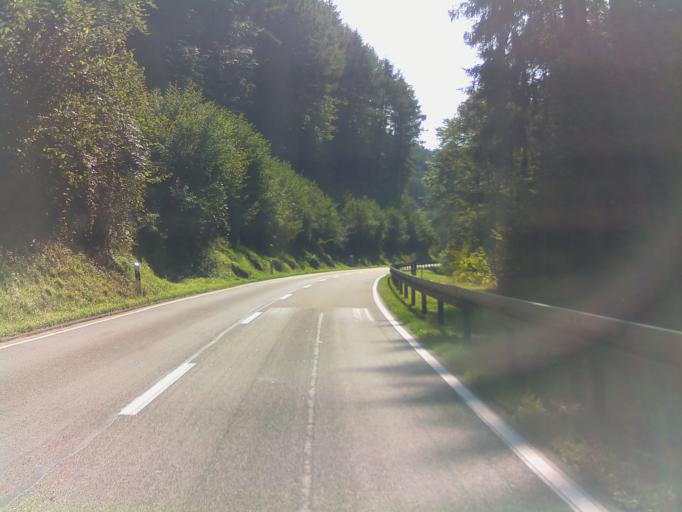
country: DE
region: Hesse
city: Hirschhorn
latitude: 49.4599
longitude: 8.8699
